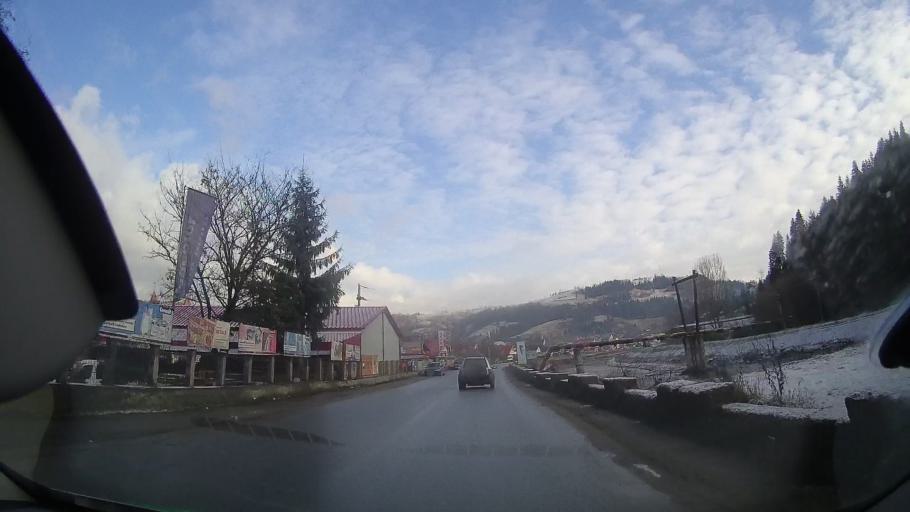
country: RO
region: Alba
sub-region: Oras Campeni
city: Campeni
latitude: 46.3591
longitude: 23.0446
